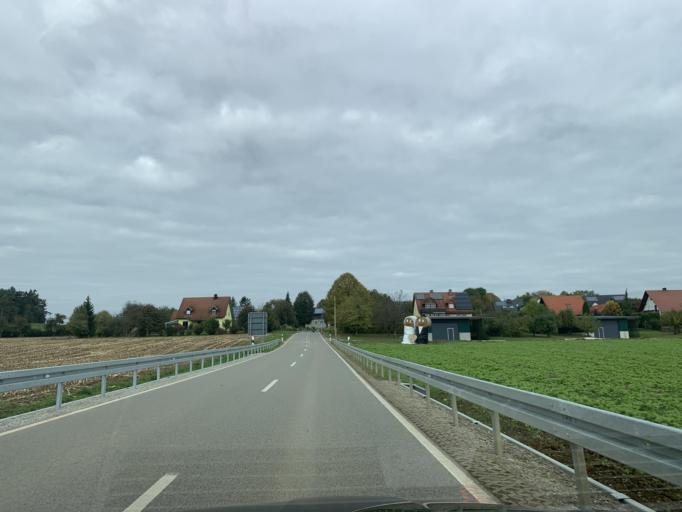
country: DE
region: Bavaria
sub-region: Upper Franconia
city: Unterleinleiter
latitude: 49.8398
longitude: 11.2457
